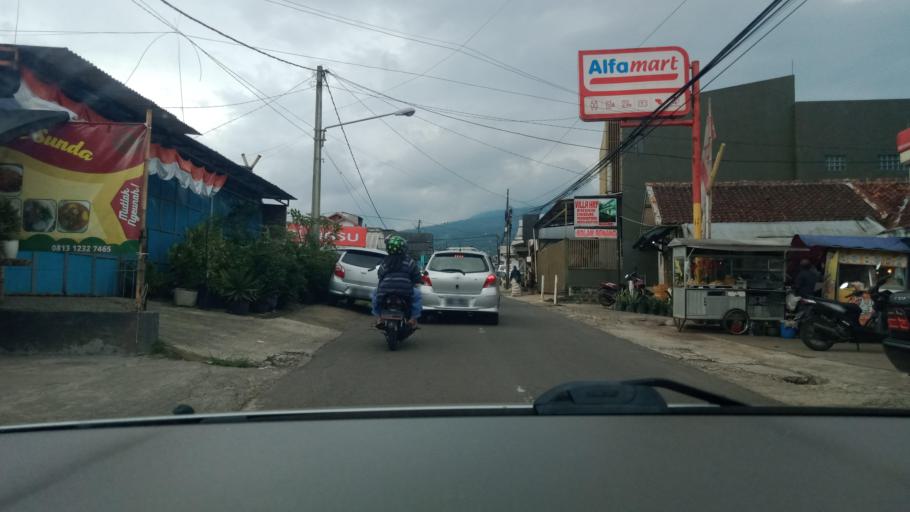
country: ID
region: West Java
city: Lembang
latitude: -6.8176
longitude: 107.5947
